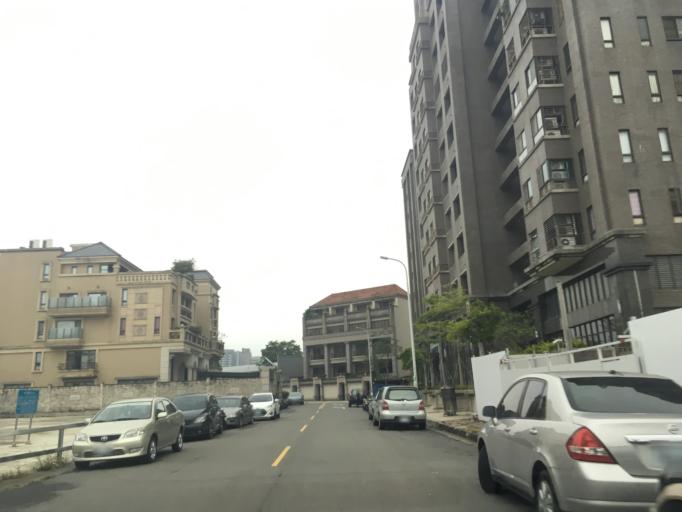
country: TW
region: Taiwan
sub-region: Taichung City
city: Taichung
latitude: 24.1653
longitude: 120.7142
